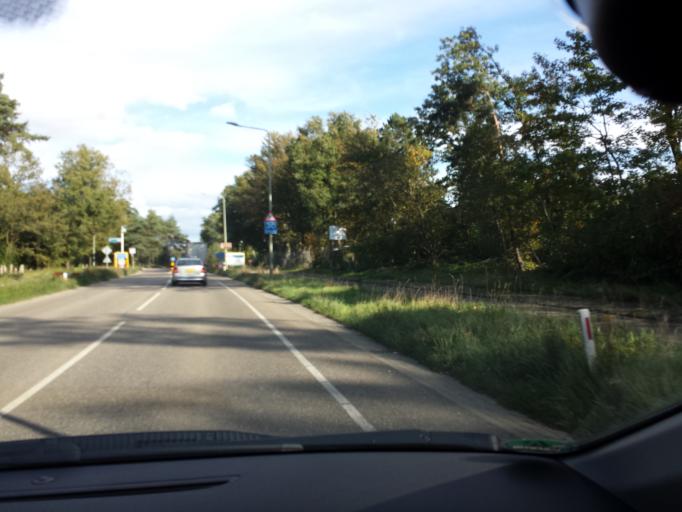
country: NL
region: Limburg
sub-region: Gemeente Onderbanken
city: Schinveld
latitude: 50.9572
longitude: 5.9887
